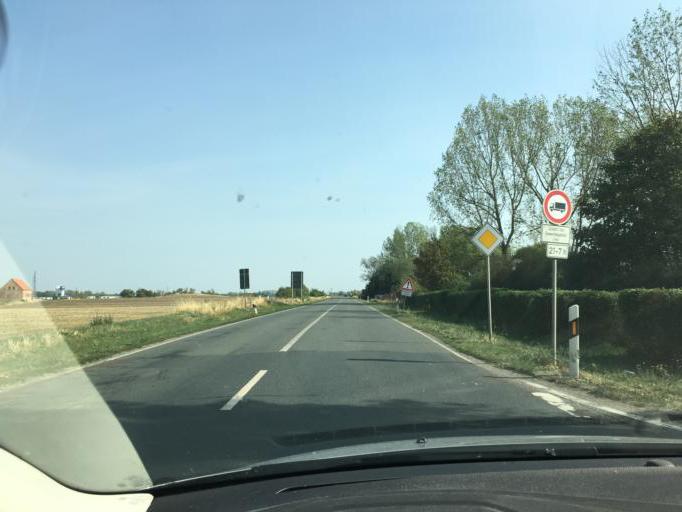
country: DE
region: Saxony-Anhalt
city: Barby
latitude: 51.9905
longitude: 11.8428
